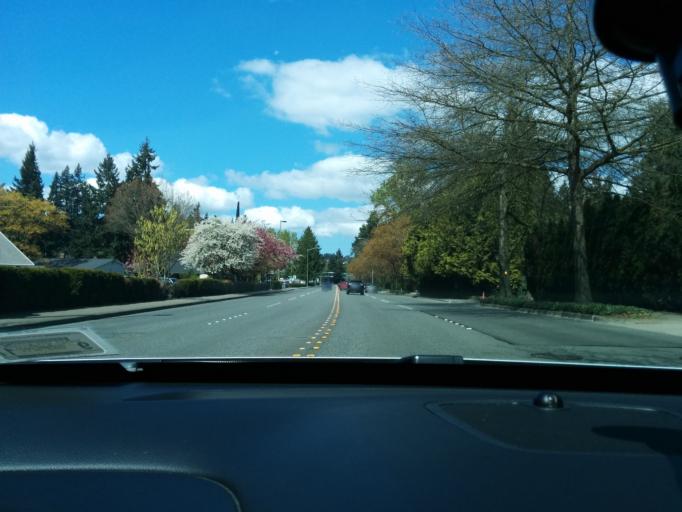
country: US
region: Washington
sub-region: King County
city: Bellevue
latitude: 47.5992
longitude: -122.1993
